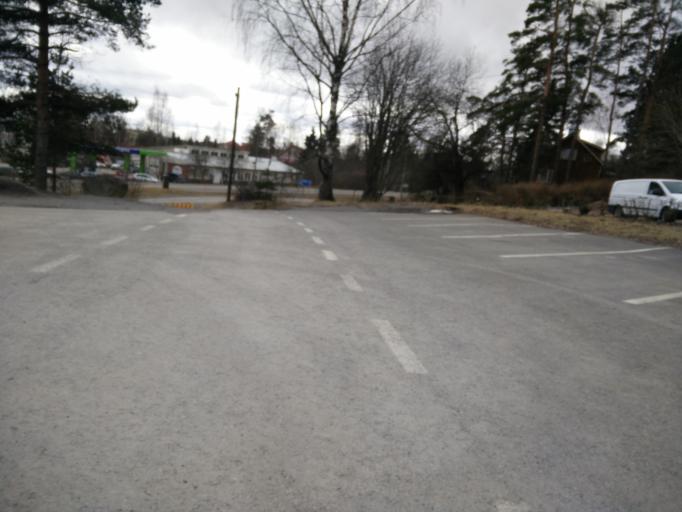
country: FI
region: Pirkanmaa
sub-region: Tampere
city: Orivesi
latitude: 61.6831
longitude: 24.3557
